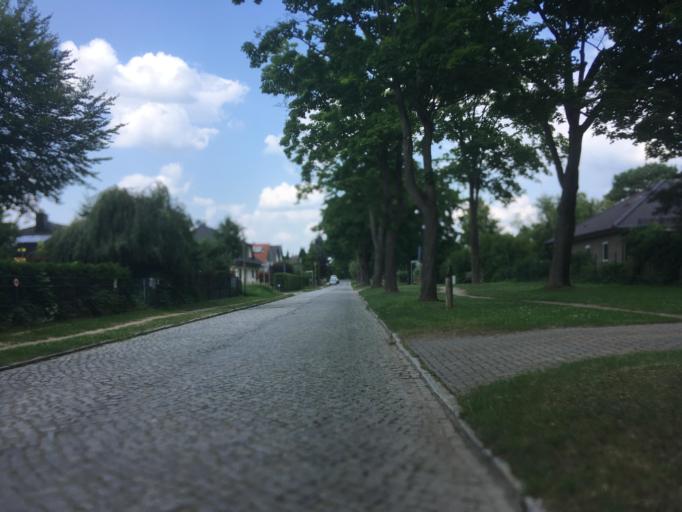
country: DE
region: Brandenburg
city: Wildau
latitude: 52.3356
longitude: 13.6240
